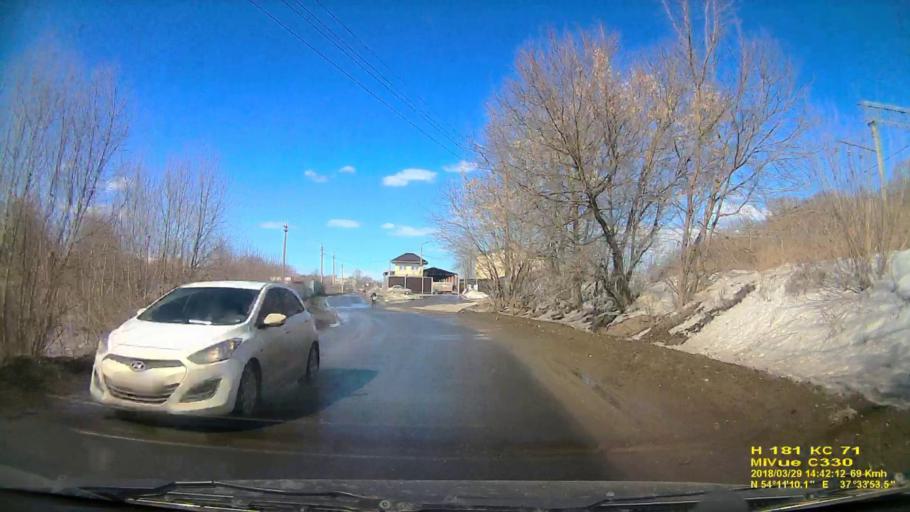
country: RU
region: Tula
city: Mendeleyevskiy
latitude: 54.1863
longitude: 37.5649
